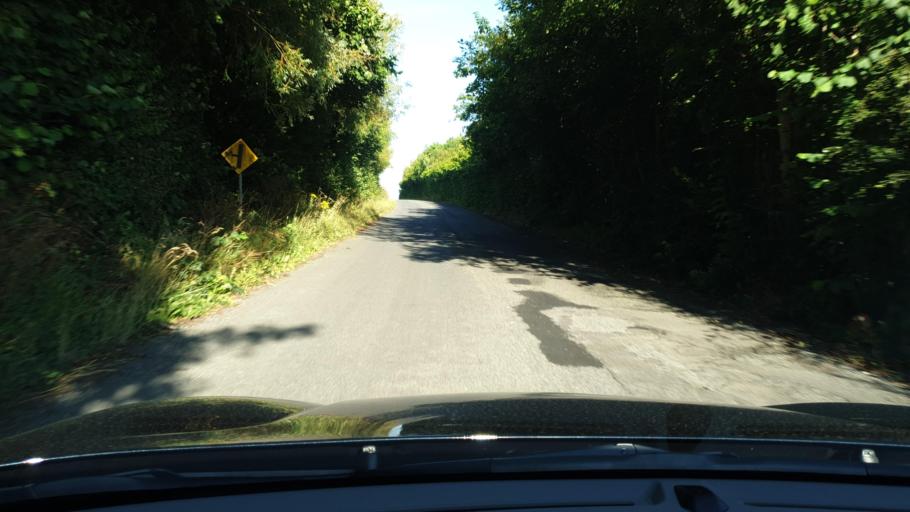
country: IE
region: Leinster
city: Balrothery
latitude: 53.5778
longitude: -6.2140
